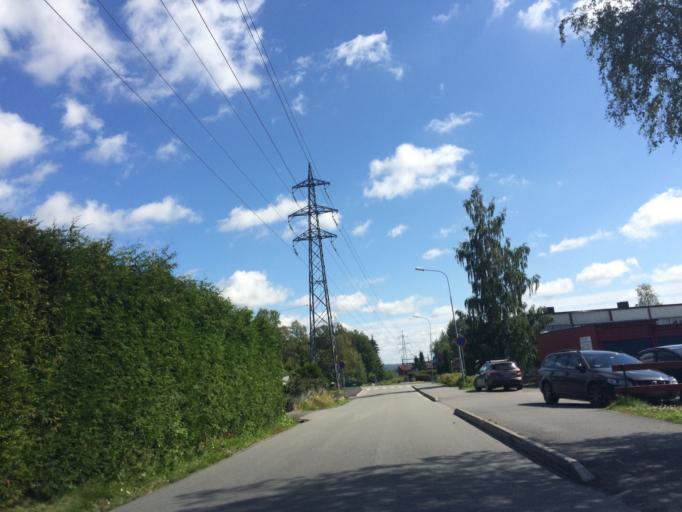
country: NO
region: Akershus
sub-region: Ski
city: Ski
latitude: 59.7153
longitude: 10.8186
